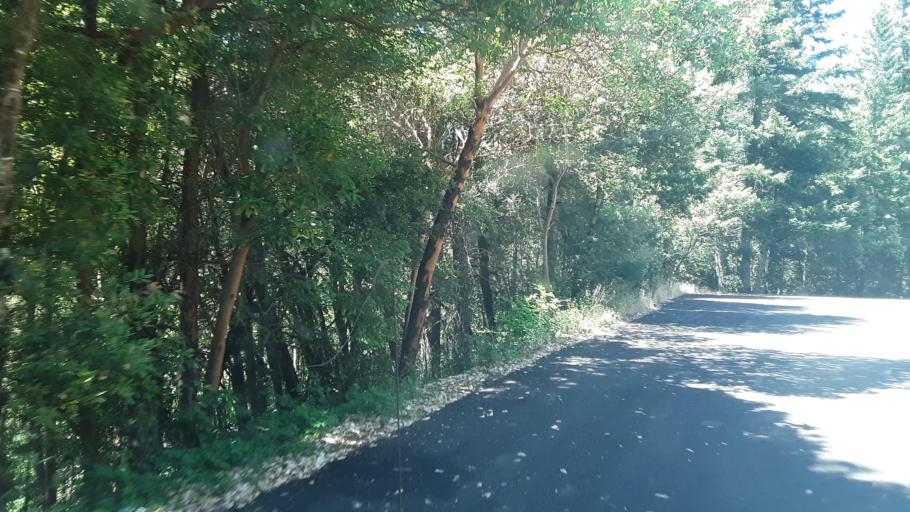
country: US
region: Oregon
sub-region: Josephine County
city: Cave Junction
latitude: 41.9659
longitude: -123.7474
